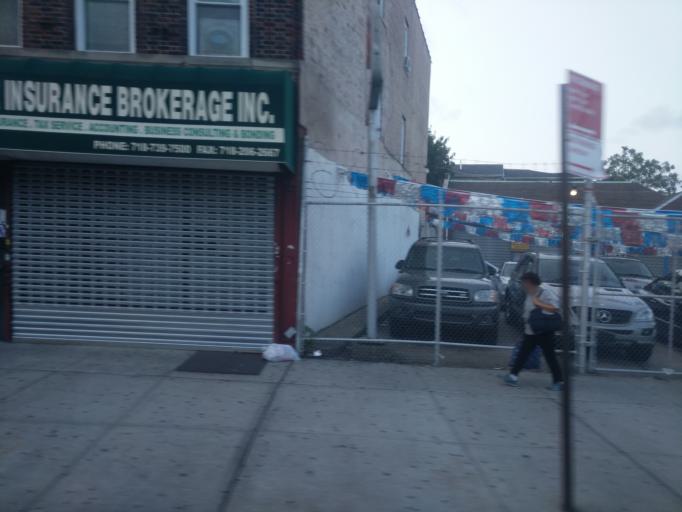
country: US
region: New York
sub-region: Queens County
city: Jamaica
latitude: 40.7053
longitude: -73.8121
